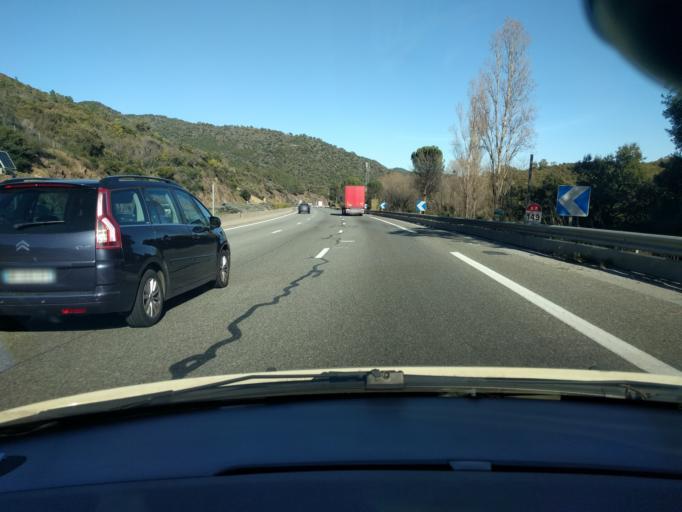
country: FR
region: Provence-Alpes-Cote d'Azur
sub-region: Departement du Var
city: Tanneron
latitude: 43.5374
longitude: 6.8446
